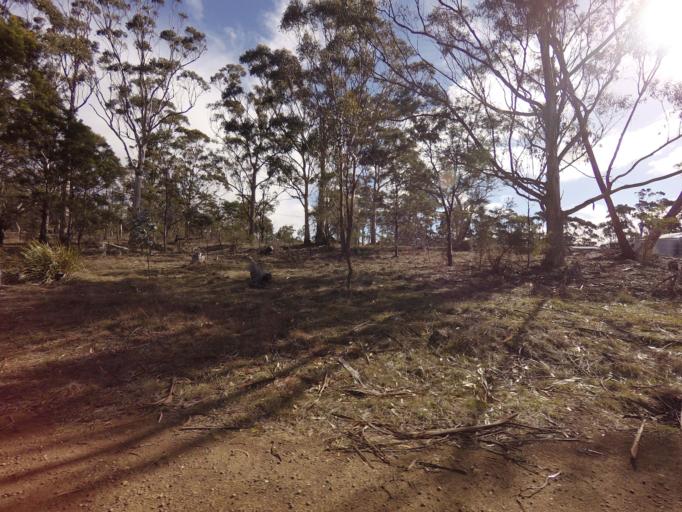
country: AU
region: Tasmania
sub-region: Sorell
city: Sorell
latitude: -42.3298
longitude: 147.9677
